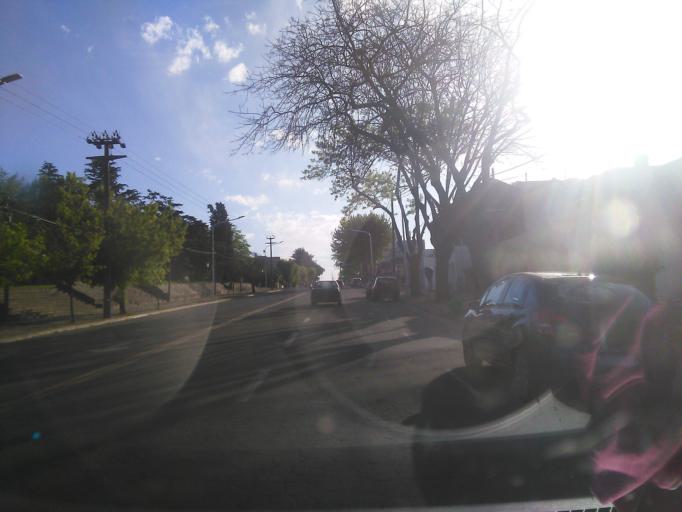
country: AR
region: Buenos Aires
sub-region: Partido de Tandil
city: Tandil
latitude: -37.3356
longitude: -59.1380
